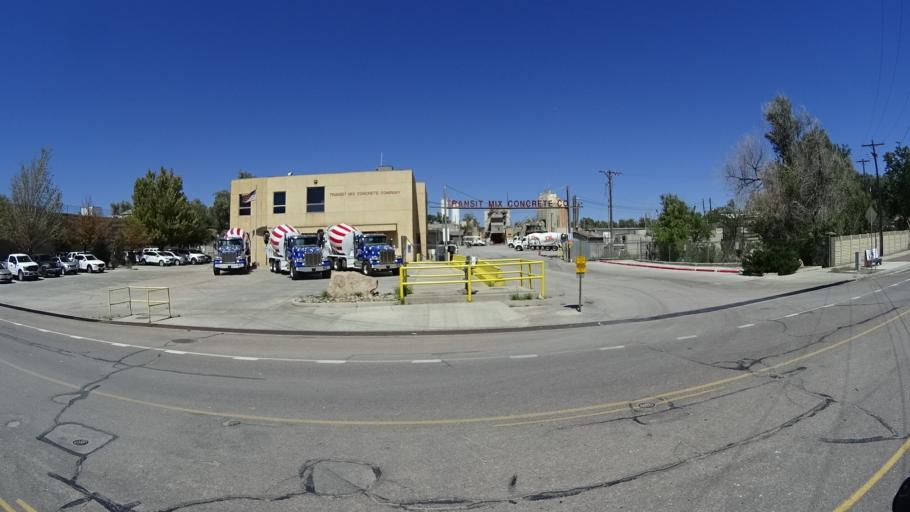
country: US
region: Colorado
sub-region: El Paso County
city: Colorado Springs
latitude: 38.8280
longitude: -104.8158
